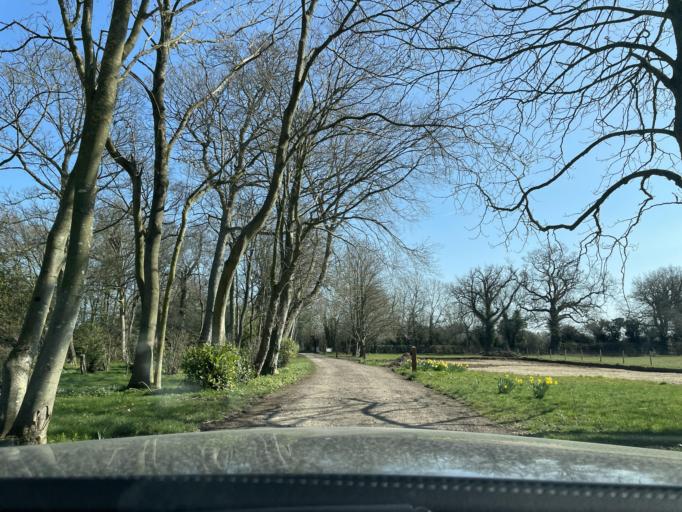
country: GB
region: England
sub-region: Norfolk
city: Hingham
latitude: 52.6211
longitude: 0.9753
